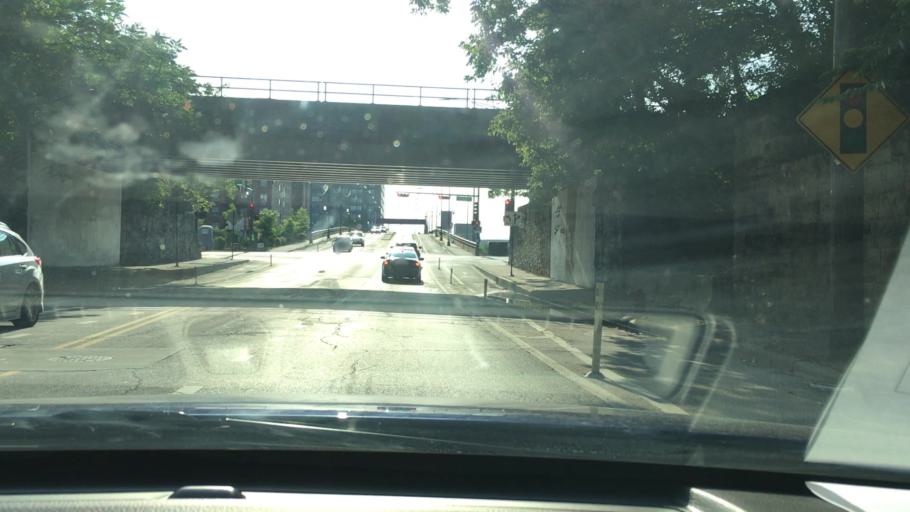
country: US
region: Illinois
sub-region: Cook County
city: Chicago
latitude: 41.8578
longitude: -87.6310
